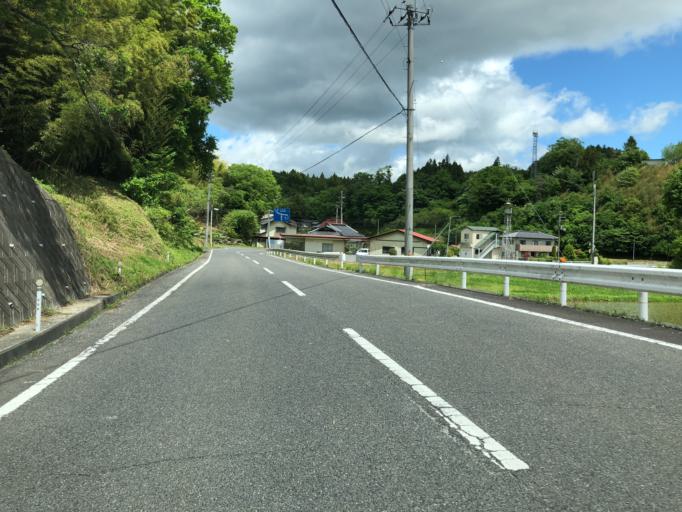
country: JP
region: Fukushima
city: Nihommatsu
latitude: 37.5366
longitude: 140.4732
